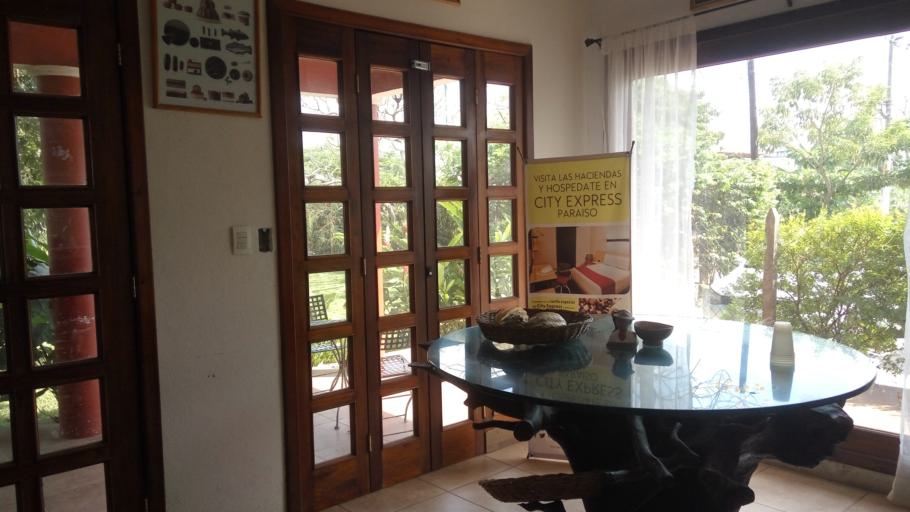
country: MX
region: Tabasco
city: Comalcalco
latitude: 18.2650
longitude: -93.2278
